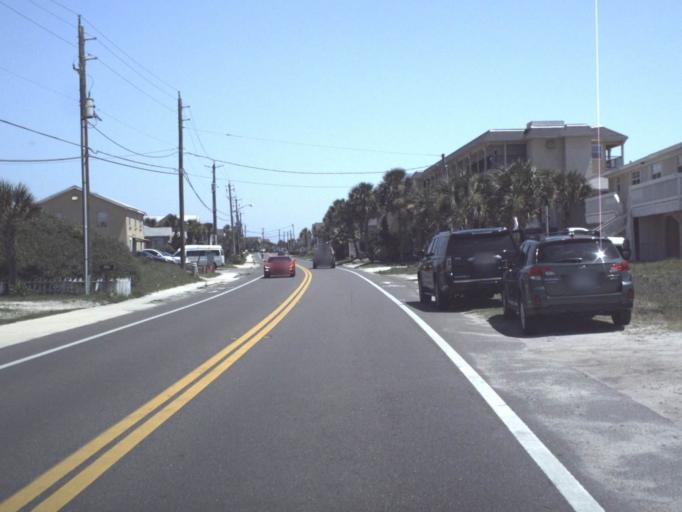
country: US
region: Florida
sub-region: Nassau County
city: Fernandina Beach
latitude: 30.6604
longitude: -81.4323
